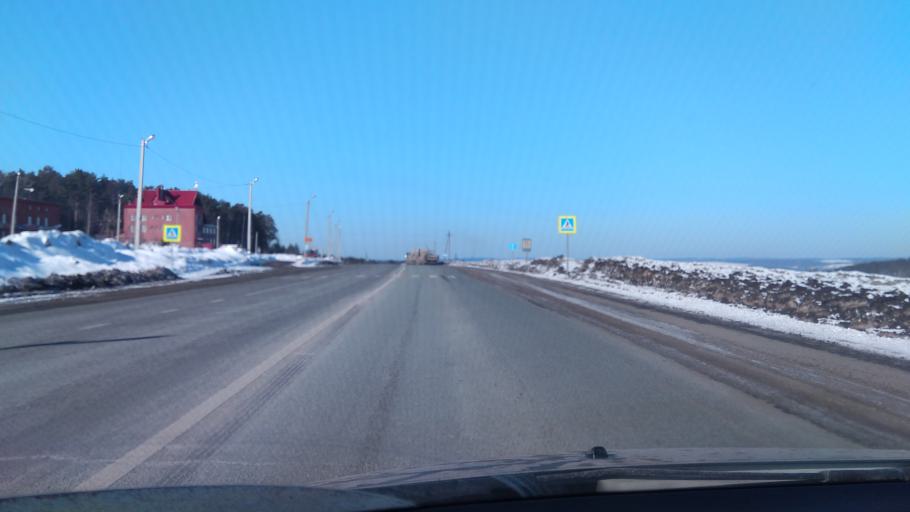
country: RU
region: Sverdlovsk
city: Bisert'
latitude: 56.8331
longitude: 58.8015
